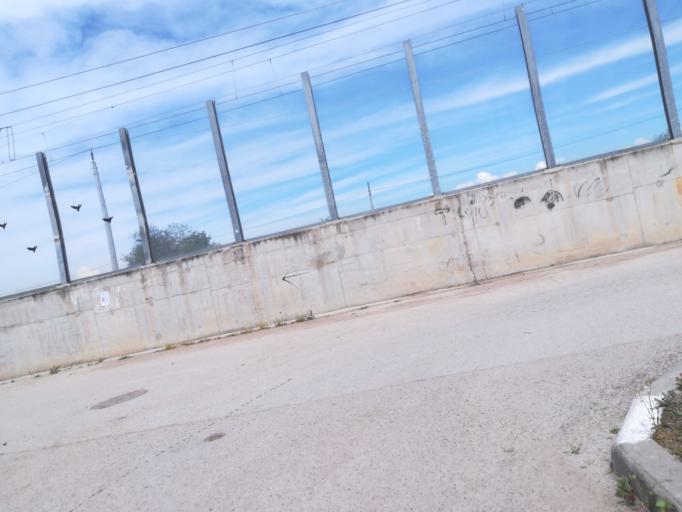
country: BG
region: Stara Zagora
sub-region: Obshtina Chirpan
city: Chirpan
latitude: 42.0988
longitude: 25.2165
